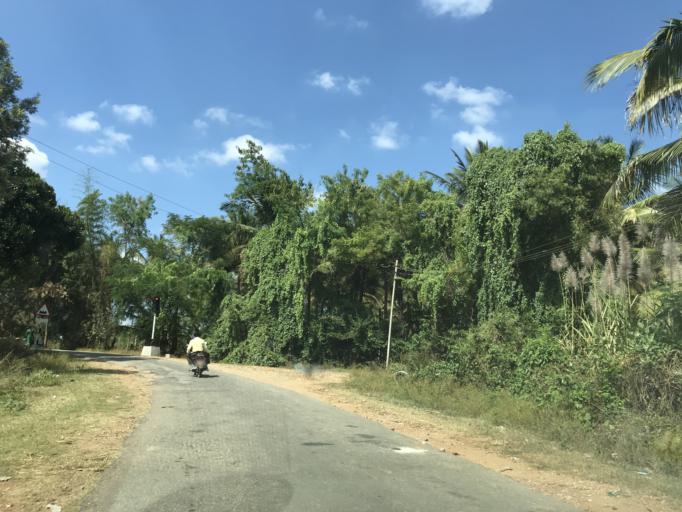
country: IN
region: Karnataka
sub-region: Mandya
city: Krishnarajpet
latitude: 12.6391
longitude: 76.3812
